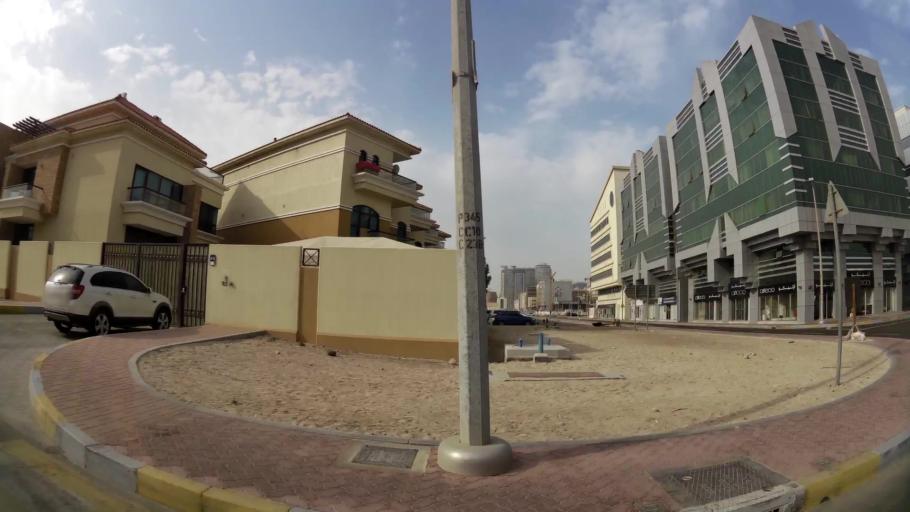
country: AE
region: Abu Dhabi
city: Abu Dhabi
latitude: 24.4783
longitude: 54.3849
